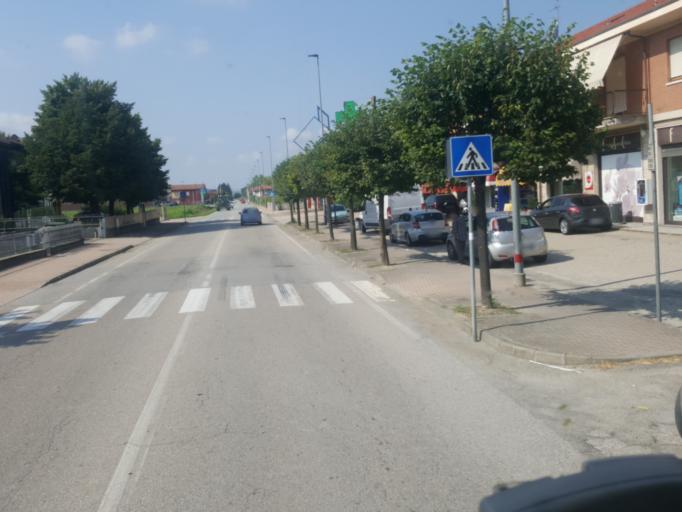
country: IT
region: Piedmont
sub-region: Provincia di Cuneo
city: Vaccheria
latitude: 44.7275
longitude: 8.0435
